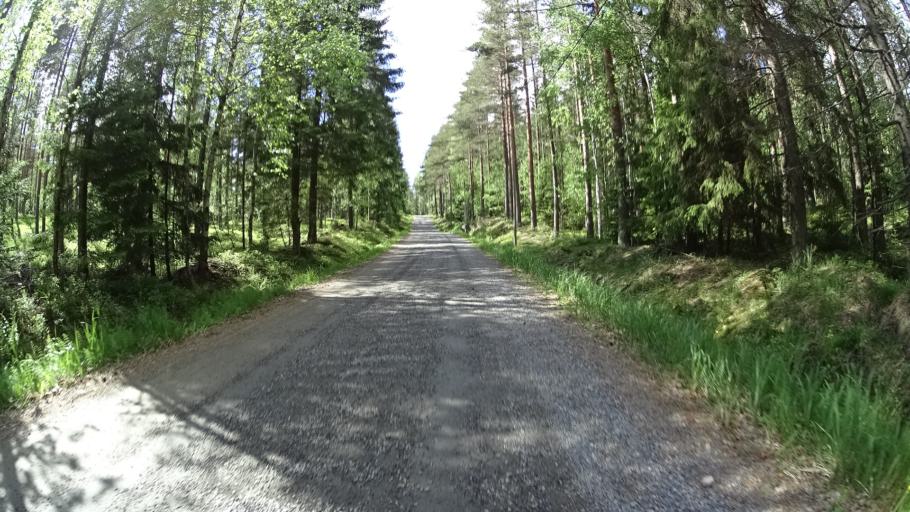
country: FI
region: Uusimaa
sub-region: Raaseporin
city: Pohja
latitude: 60.1849
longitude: 23.5807
